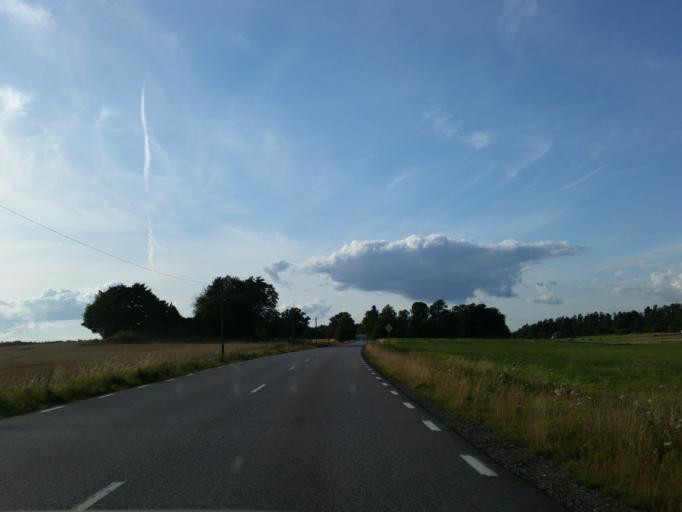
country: SE
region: Stockholm
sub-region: Sodertalje Kommun
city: Molnbo
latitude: 58.9950
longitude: 17.4118
